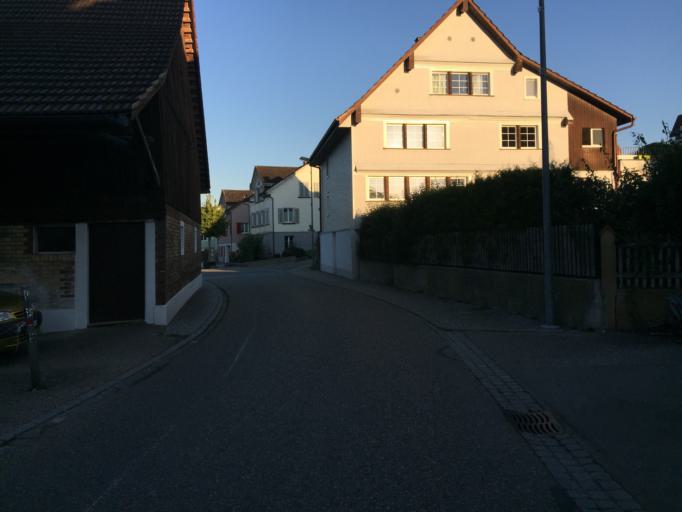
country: CH
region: Saint Gallen
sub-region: Wahlkreis Wil
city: Oberuzwil
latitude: 47.4209
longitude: 9.1359
